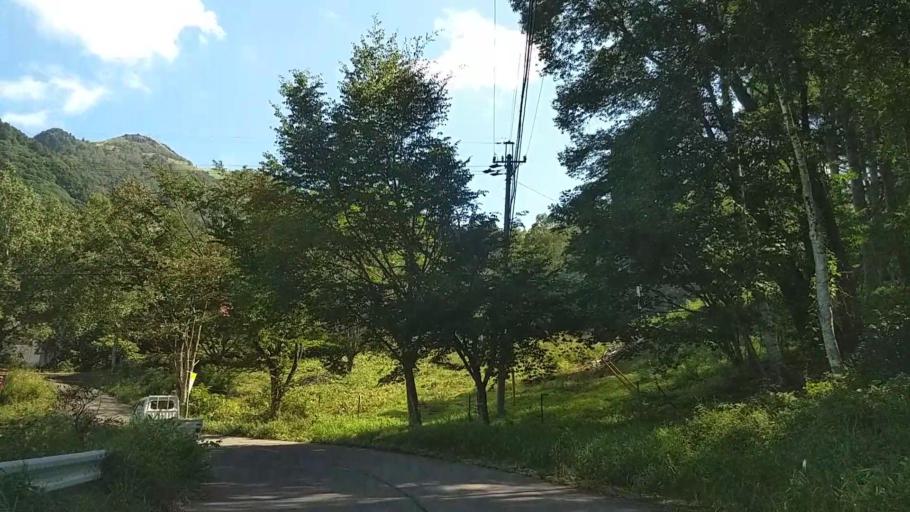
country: JP
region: Nagano
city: Matsumoto
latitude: 36.2083
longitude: 138.1024
